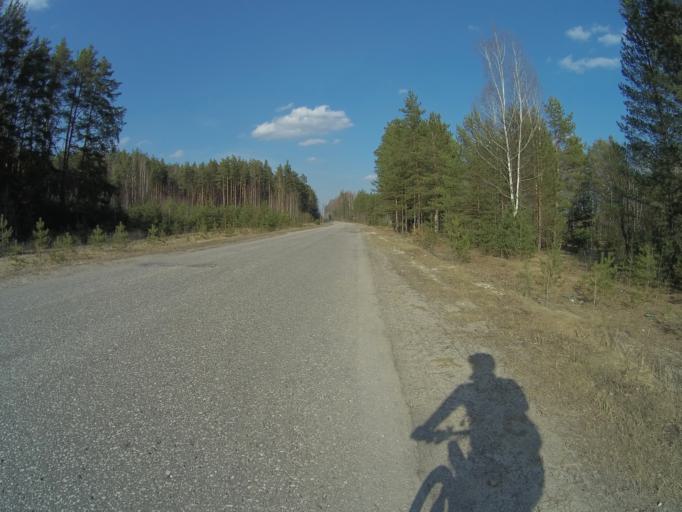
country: RU
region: Vladimir
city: Sudogda
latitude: 56.0823
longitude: 40.7785
